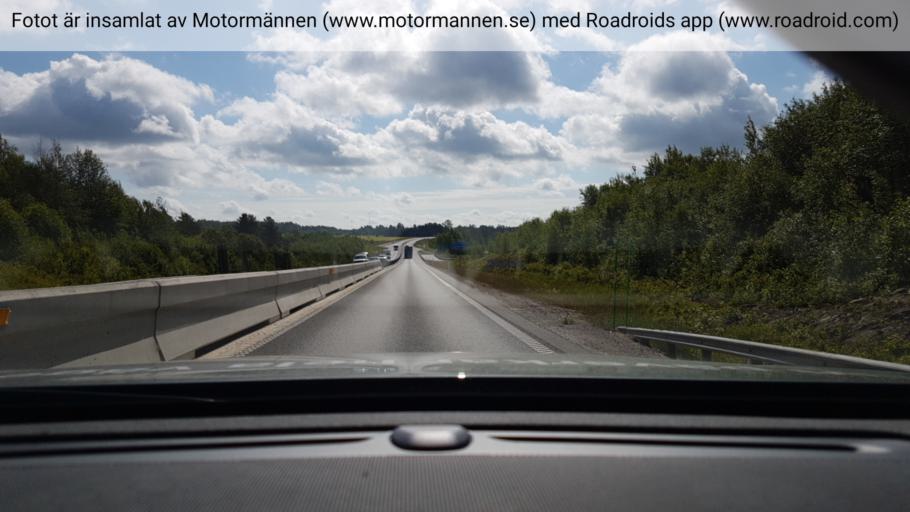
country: SE
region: Vaesterbotten
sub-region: Umea Kommun
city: Roback
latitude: 63.8860
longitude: 20.0265
